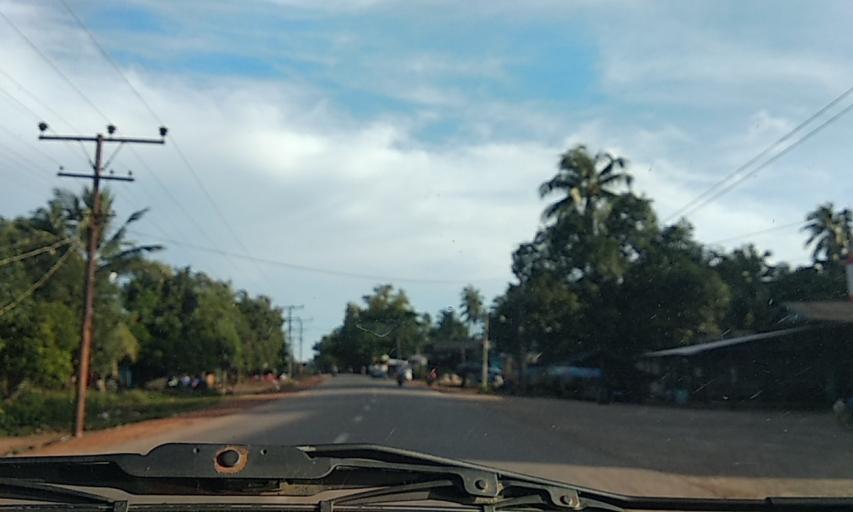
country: MM
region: Mon
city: Mawlamyine
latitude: 16.4099
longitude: 97.7006
